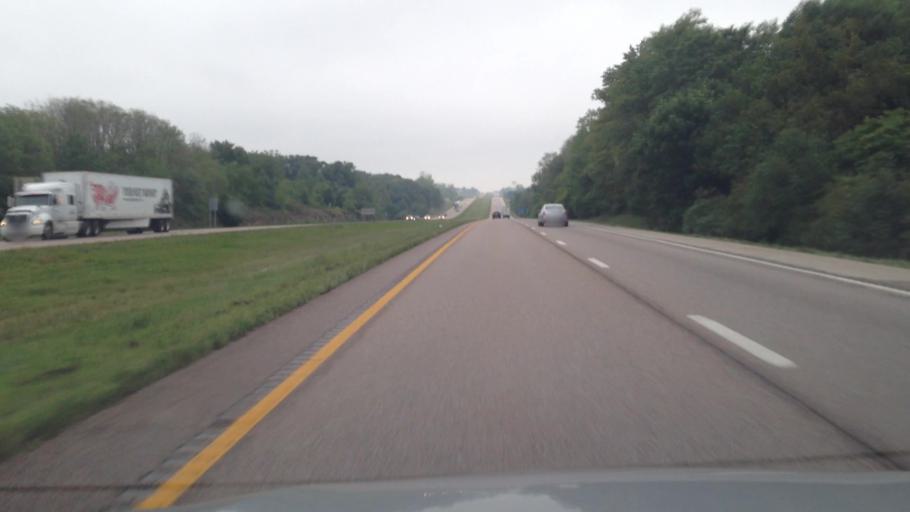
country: US
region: Missouri
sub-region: Clinton County
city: Lathrop
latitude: 39.4739
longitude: -94.3121
